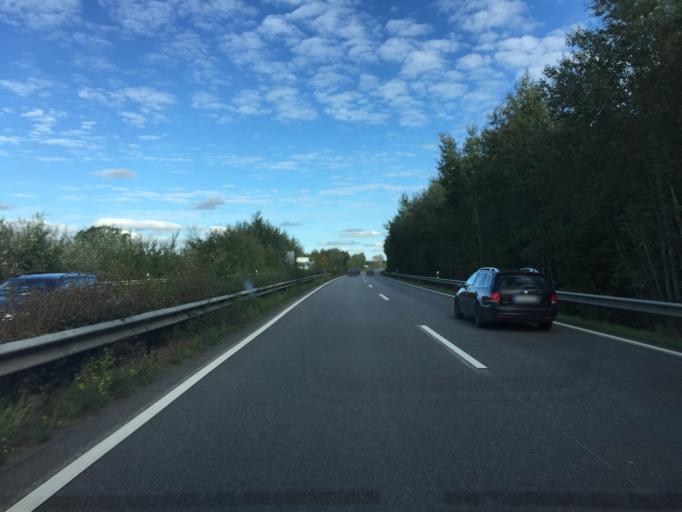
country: DE
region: Schleswig-Holstein
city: Neustadt in Holstein
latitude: 54.1144
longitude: 10.7852
